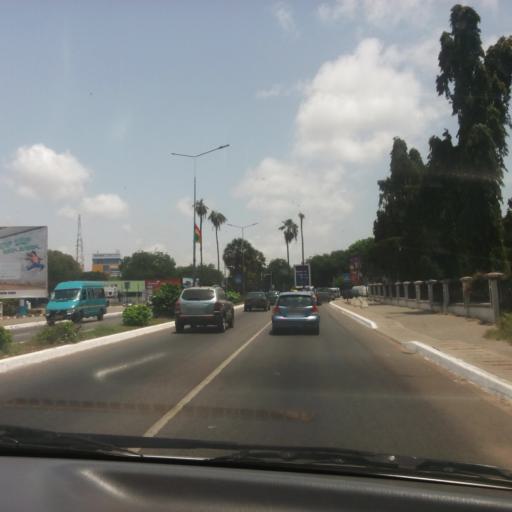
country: GH
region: Greater Accra
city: Accra
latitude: 5.5586
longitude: -0.1977
